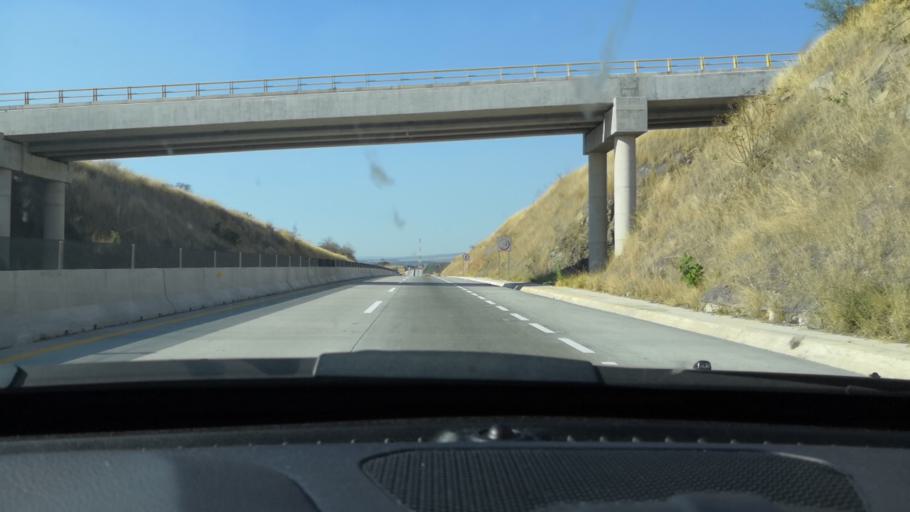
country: MX
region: Jalisco
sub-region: Zapotlanejo
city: La Mezquitera
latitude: 20.5923
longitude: -103.0997
